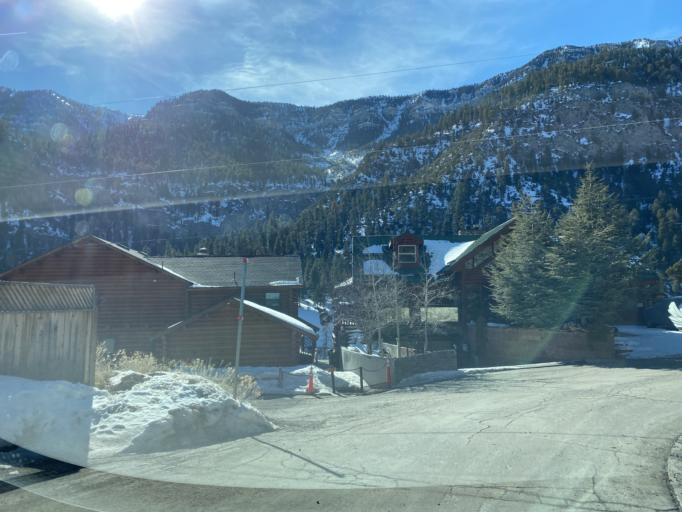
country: US
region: Nevada
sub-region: Nye County
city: Pahrump
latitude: 36.2620
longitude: -115.6503
